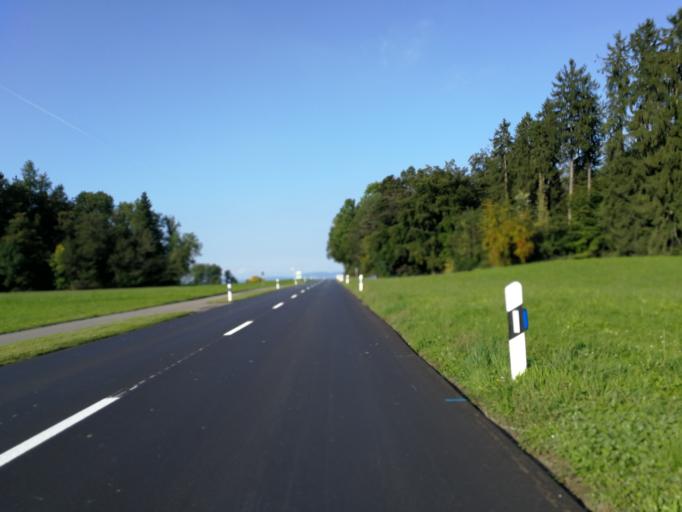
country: CH
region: Zurich
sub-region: Bezirk Meilen
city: Oetwil am See
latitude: 47.2608
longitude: 8.7222
